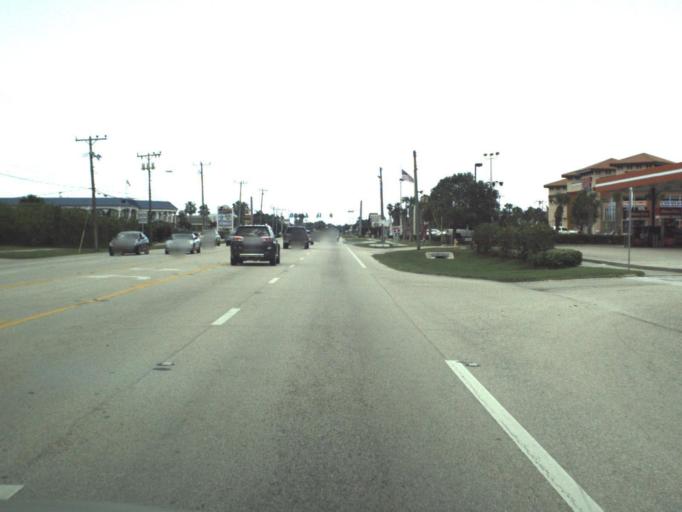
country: US
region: Florida
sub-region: Brevard County
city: Cape Canaveral
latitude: 28.3986
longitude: -80.6144
